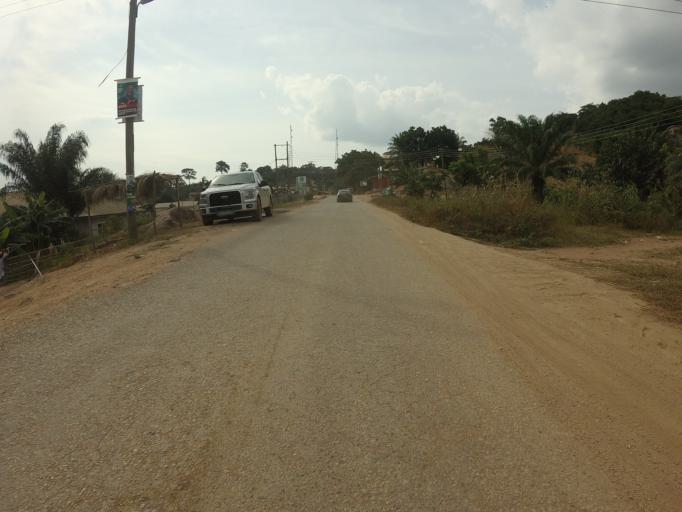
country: GH
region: Volta
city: Ho
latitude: 6.6836
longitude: 0.3347
